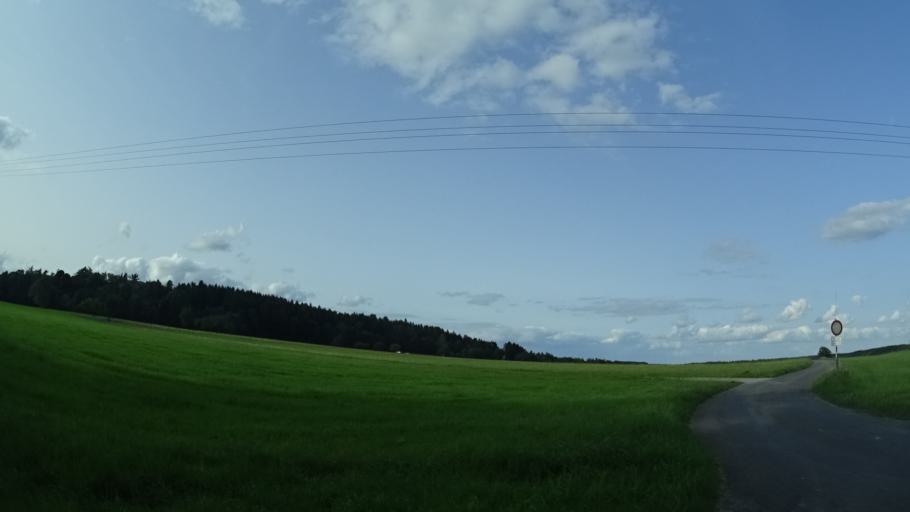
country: DE
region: Baden-Wuerttemberg
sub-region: Karlsruhe Region
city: Mudau
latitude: 49.5433
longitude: 9.1387
